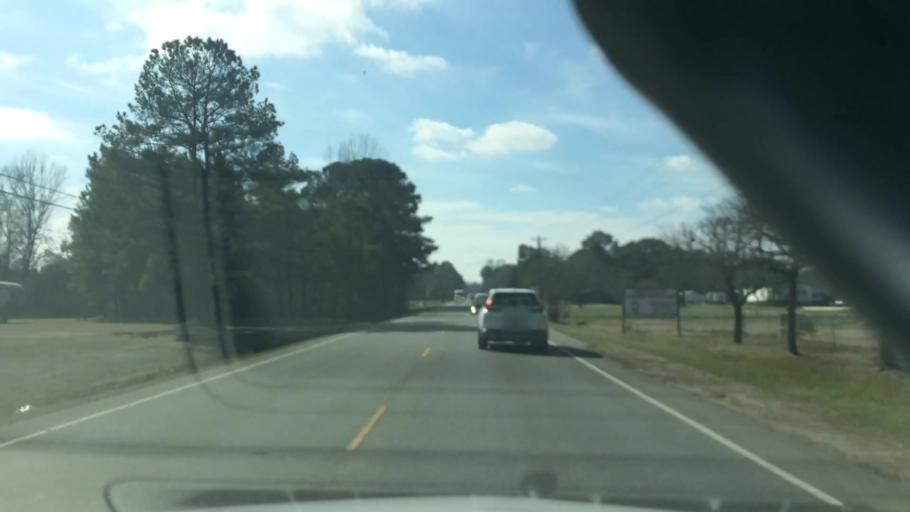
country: US
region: North Carolina
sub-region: Duplin County
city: Wallace
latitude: 34.7728
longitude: -77.9210
